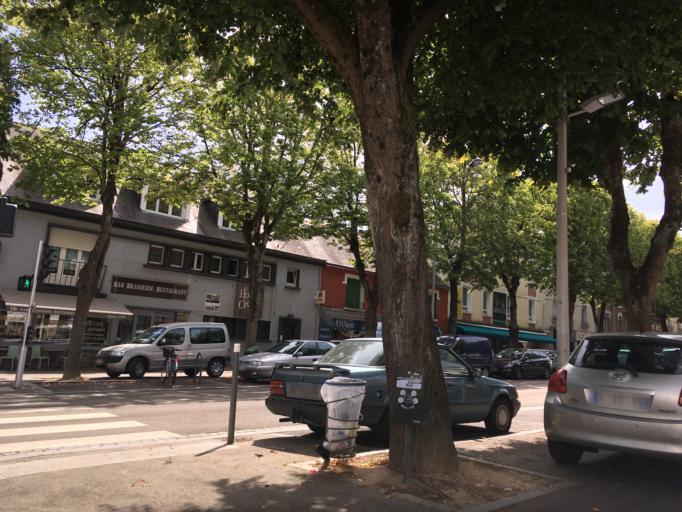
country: FR
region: Brittany
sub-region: Departement du Morbihan
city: Lorient
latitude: 47.7454
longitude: -3.3734
